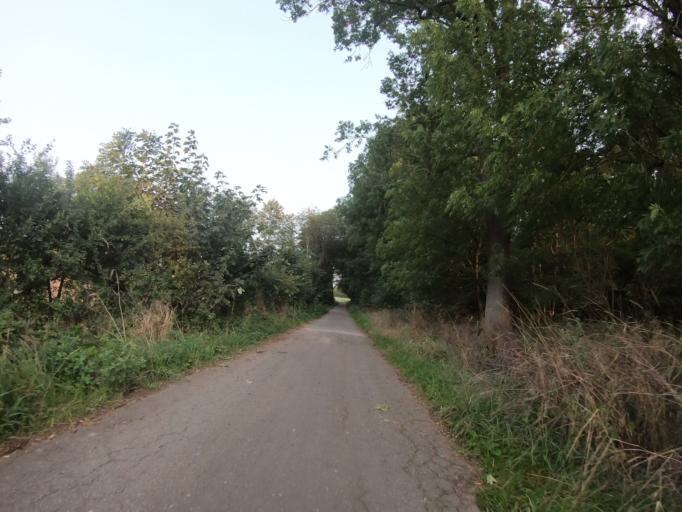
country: DE
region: Lower Saxony
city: Leiferde
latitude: 52.4309
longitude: 10.4609
